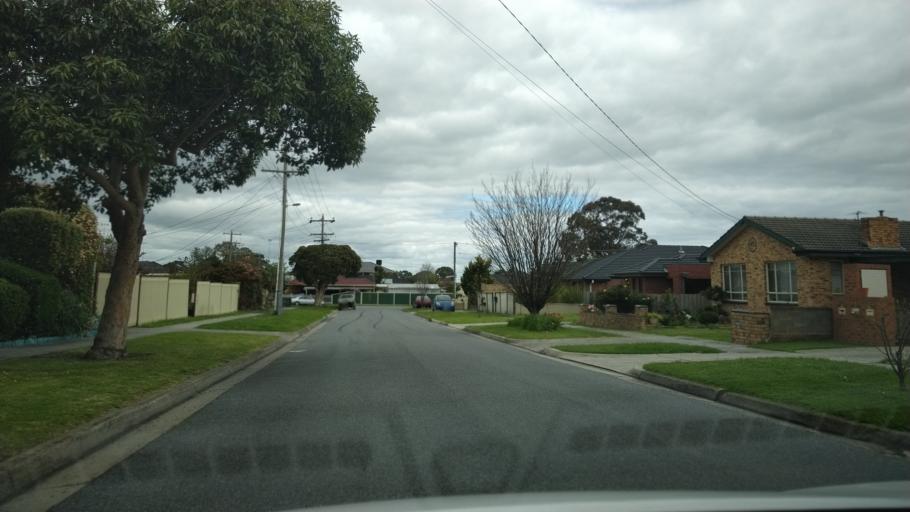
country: AU
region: Victoria
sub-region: Greater Dandenong
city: Noble Park
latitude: -37.9740
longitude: 145.1690
